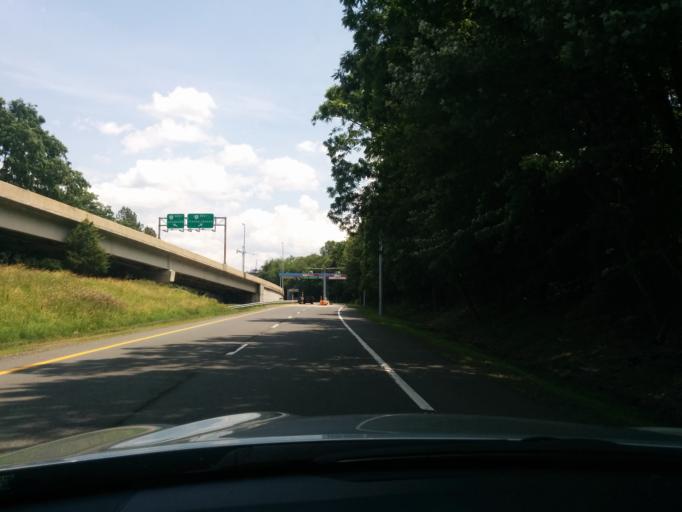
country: US
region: Virginia
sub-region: Fairfax County
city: Tysons Corner
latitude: 38.9326
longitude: -77.2488
